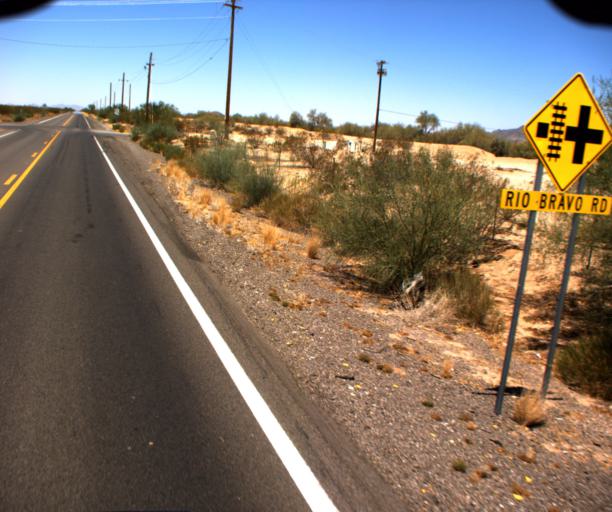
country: US
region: Arizona
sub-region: Pinal County
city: Maricopa
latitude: 33.0777
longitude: -112.1499
